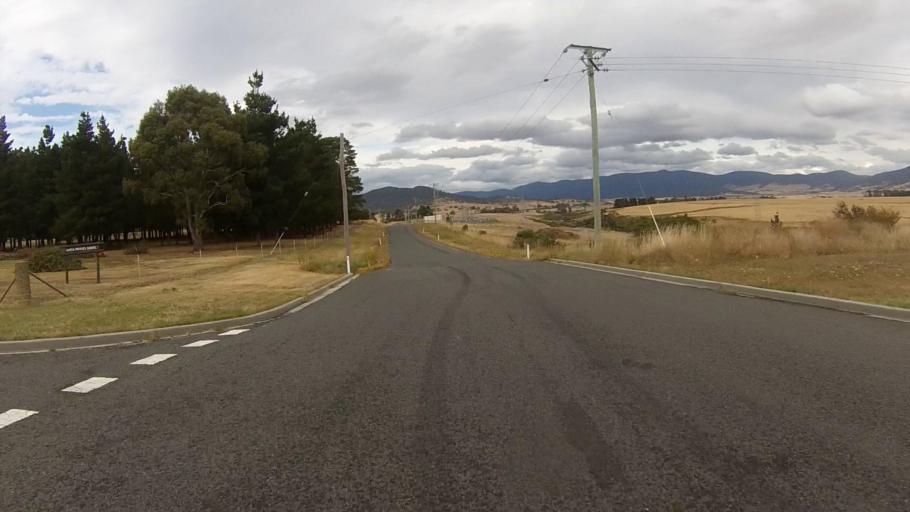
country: AU
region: Tasmania
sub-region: Northern Midlands
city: Evandale
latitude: -41.7833
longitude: 147.7238
